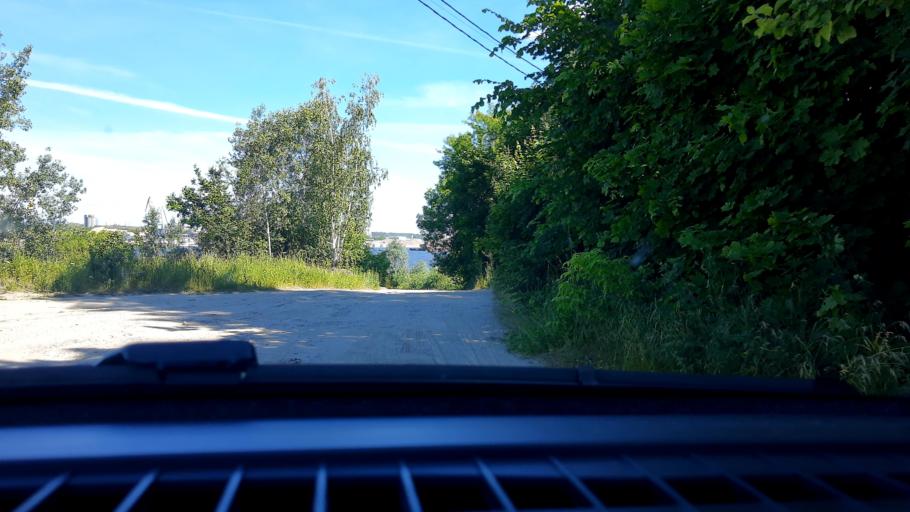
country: RU
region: Nizjnij Novgorod
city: Nizhniy Novgorod
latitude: 56.2249
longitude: 43.9138
